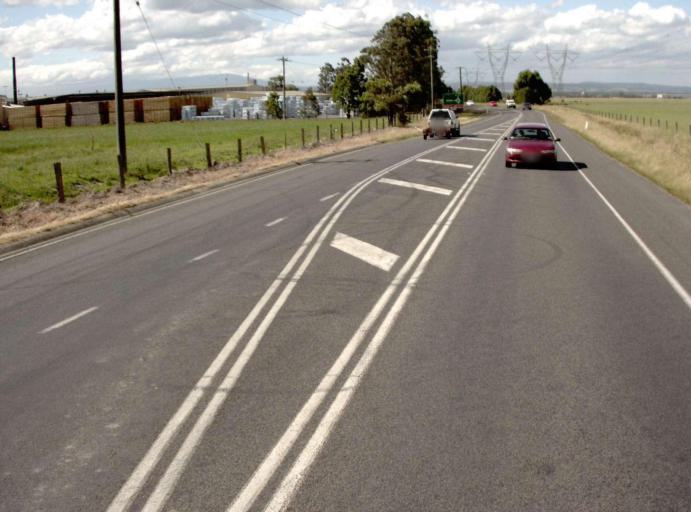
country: AU
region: Victoria
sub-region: Latrobe
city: Morwell
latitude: -38.2668
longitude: 146.4344
